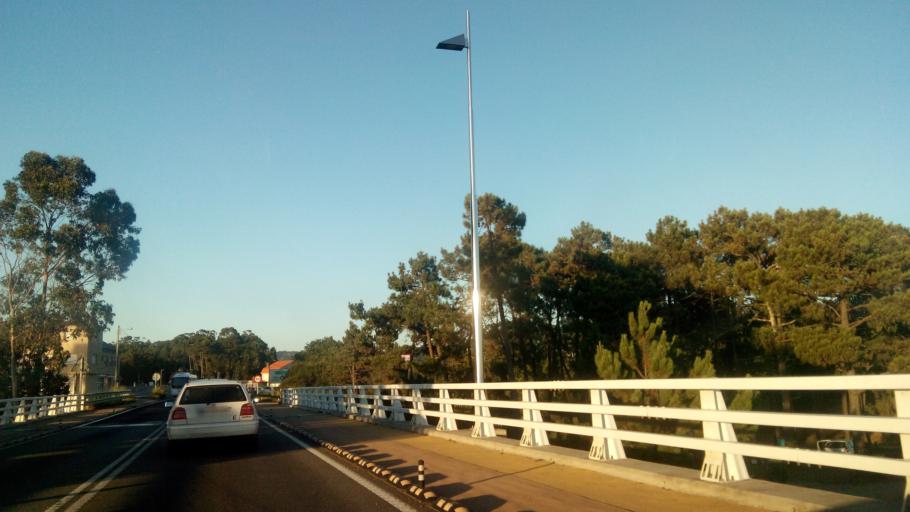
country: ES
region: Galicia
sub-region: Provincia de Pontevedra
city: Vilanova de Arousa
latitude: 42.5487
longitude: -8.8331
